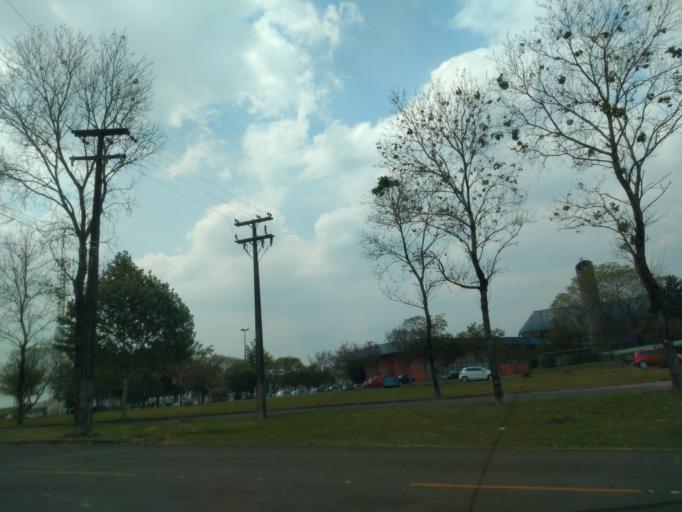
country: BR
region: Parana
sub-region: Guarapuava
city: Guarapuava
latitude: -25.3789
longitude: -51.4793
